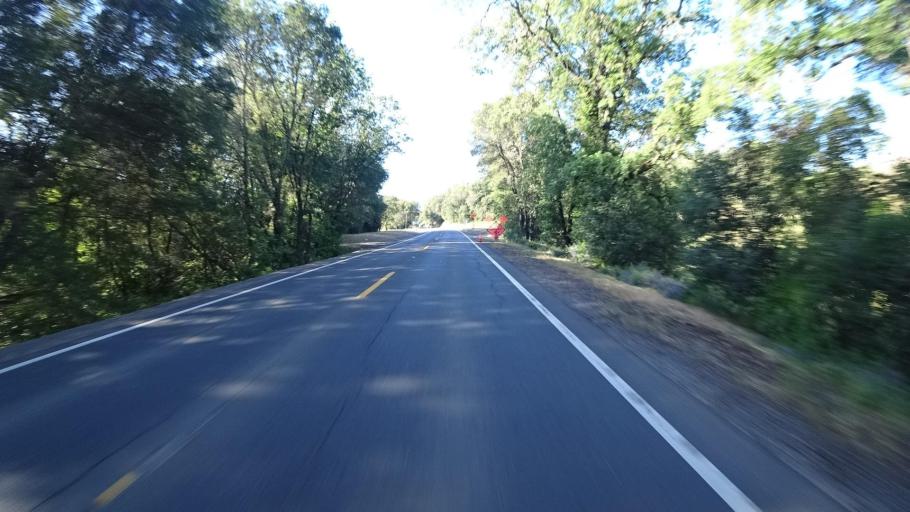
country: US
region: California
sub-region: Lake County
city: Upper Lake
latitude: 39.1554
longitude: -122.9209
